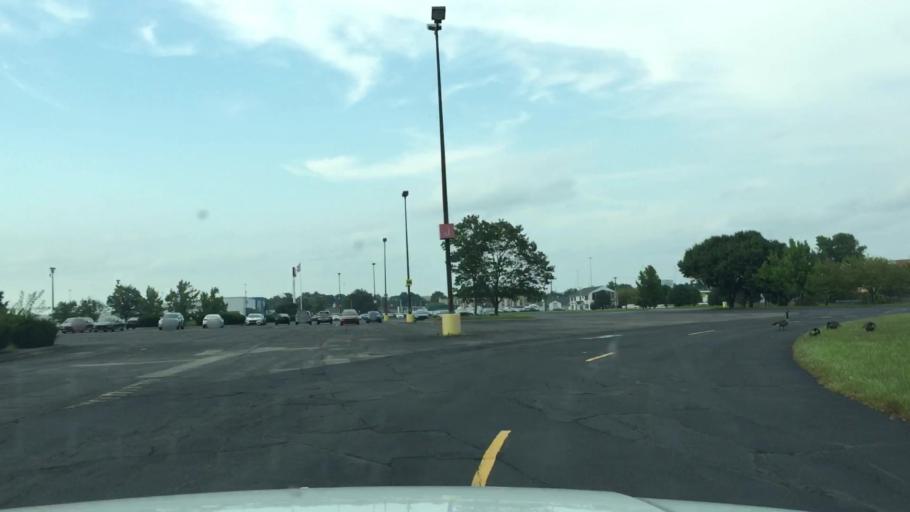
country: US
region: Ohio
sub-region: Franklin County
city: Blacklick Estates
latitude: 39.9249
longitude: -82.8342
